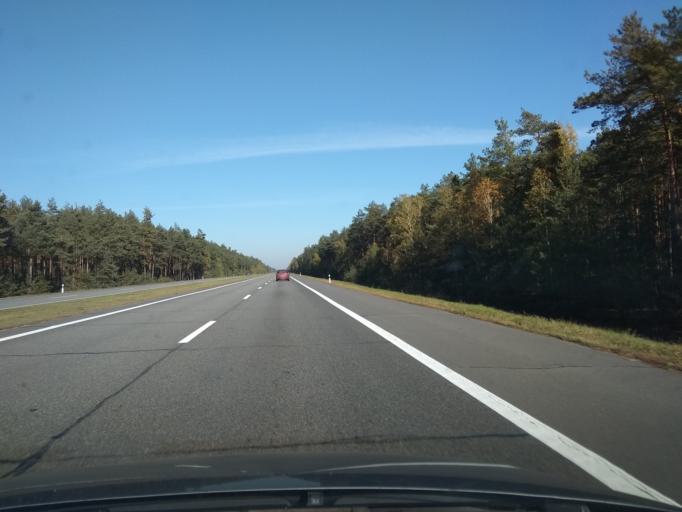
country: BY
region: Grodnenskaya
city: Zhyrovichy
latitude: 52.9329
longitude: 25.6992
